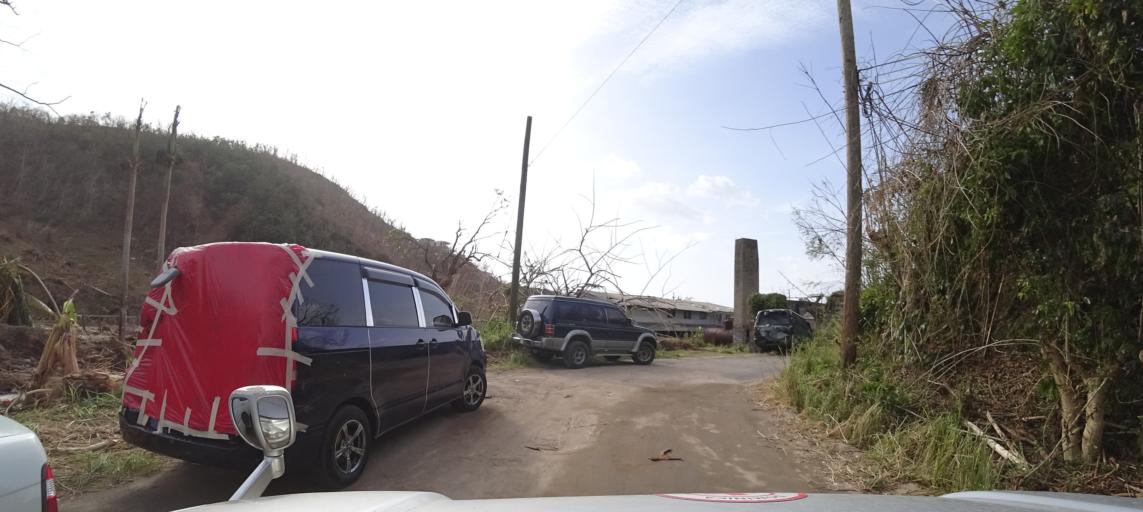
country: DM
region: Saint George
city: Roseau
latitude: 15.3270
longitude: -61.3863
